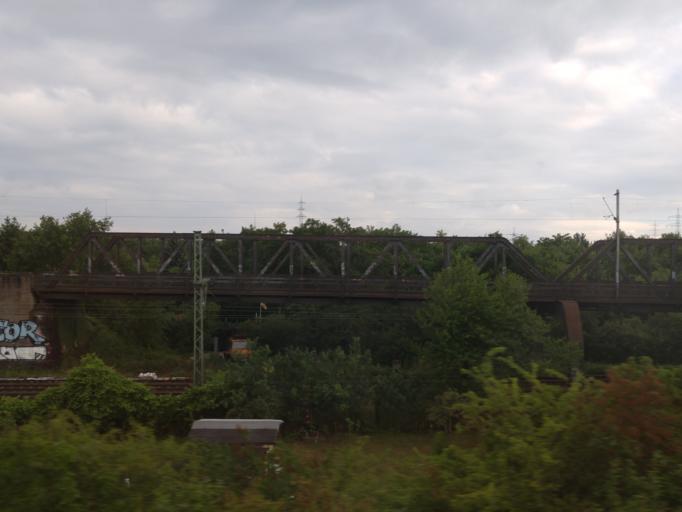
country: DE
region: Hesse
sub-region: Regierungsbezirk Darmstadt
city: Darmstadt
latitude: 49.8910
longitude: 8.6332
